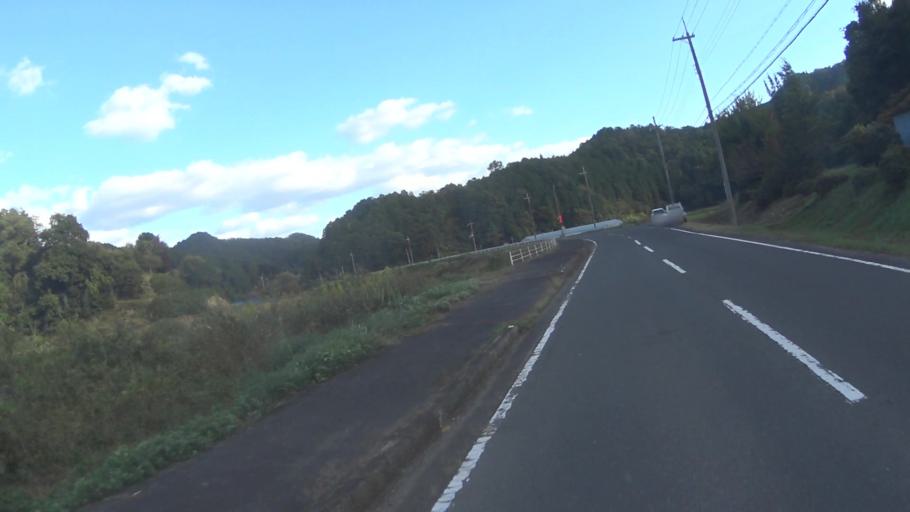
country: JP
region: Kyoto
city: Miyazu
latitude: 35.4390
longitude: 135.2179
